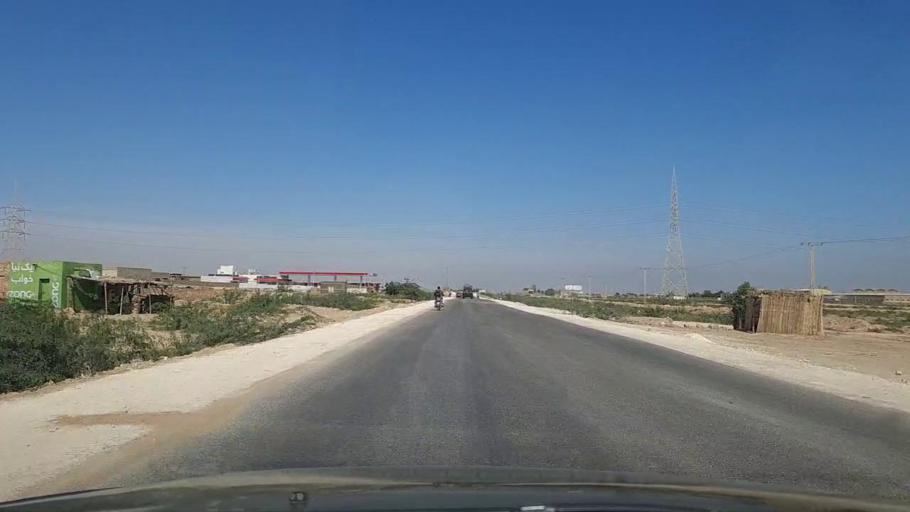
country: PK
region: Sindh
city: Kotri
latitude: 25.3317
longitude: 68.2423
